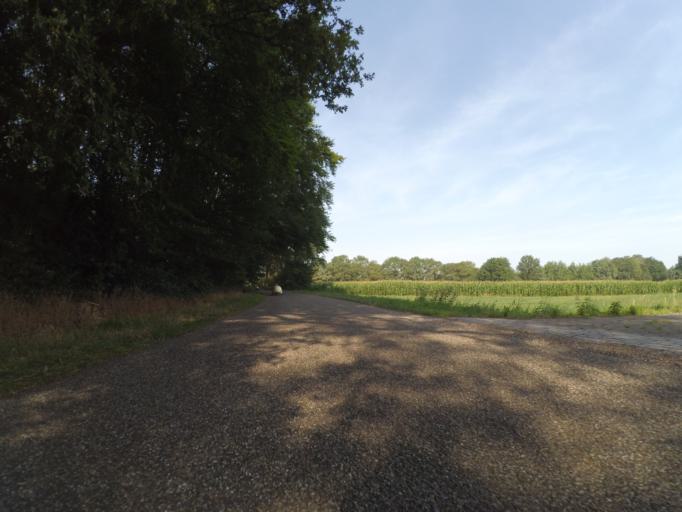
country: DE
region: Lower Saxony
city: Getelo
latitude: 52.3841
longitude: 6.8744
